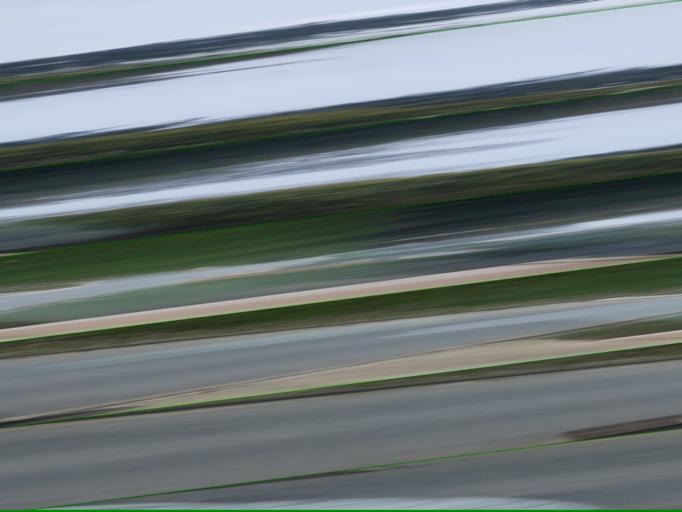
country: FR
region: Ile-de-France
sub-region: Departement des Yvelines
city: Houdan
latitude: 48.8376
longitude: 1.6081
